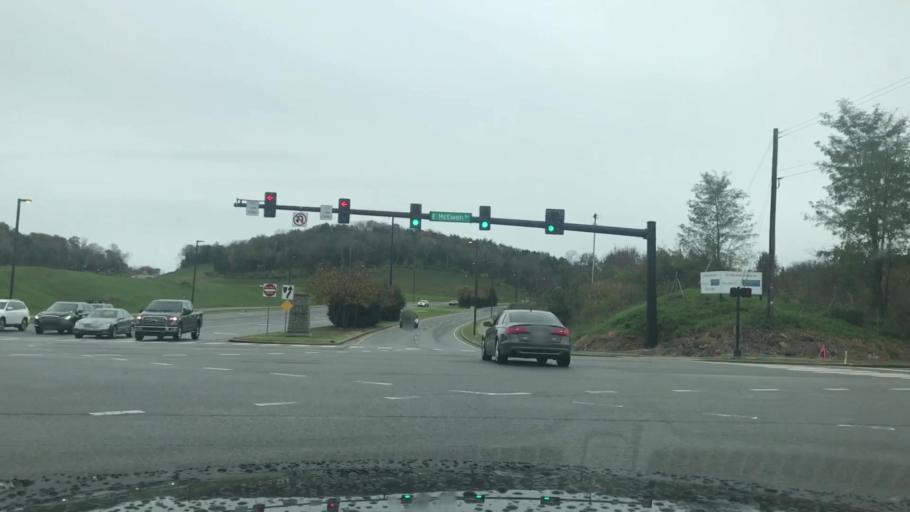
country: US
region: Tennessee
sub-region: Williamson County
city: Franklin
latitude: 35.9331
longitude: -86.8118
